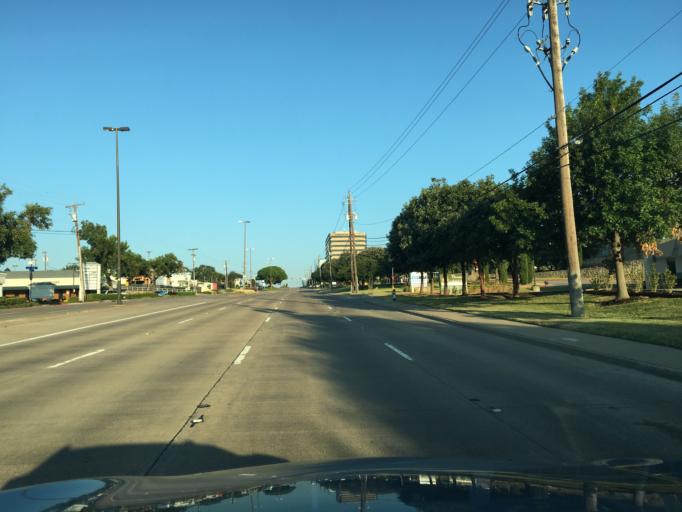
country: US
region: Texas
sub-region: Dallas County
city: Addison
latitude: 32.9541
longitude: -96.8146
